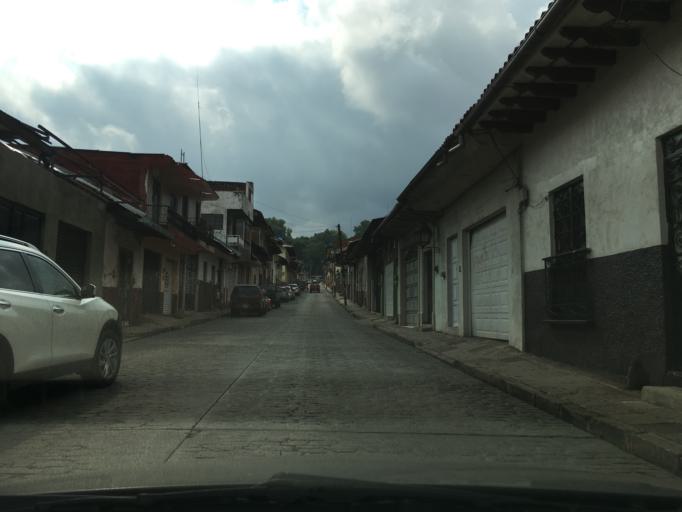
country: MX
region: Michoacan
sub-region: Uruapan
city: Uruapan
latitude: 19.4233
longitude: -102.0680
